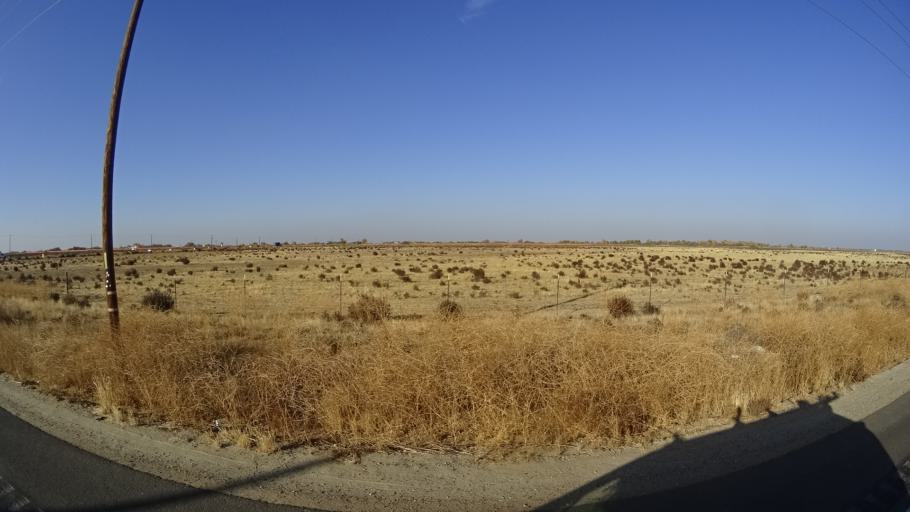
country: US
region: California
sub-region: Kern County
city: Rosedale
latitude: 35.2962
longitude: -119.2507
